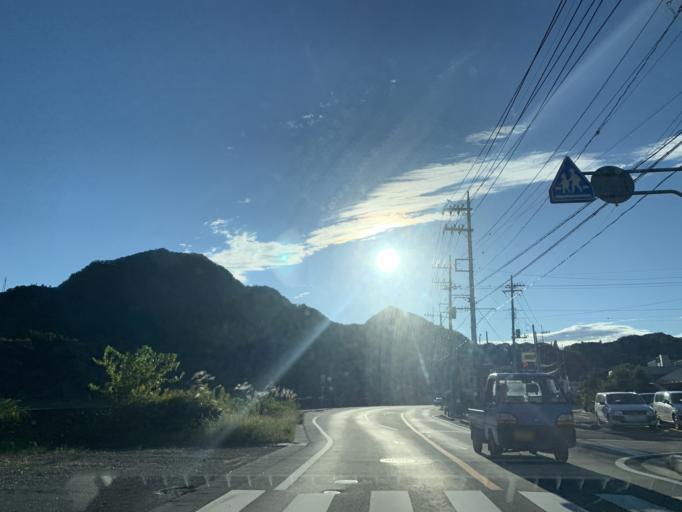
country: JP
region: Yamanashi
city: Uenohara
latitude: 35.6169
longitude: 139.1149
